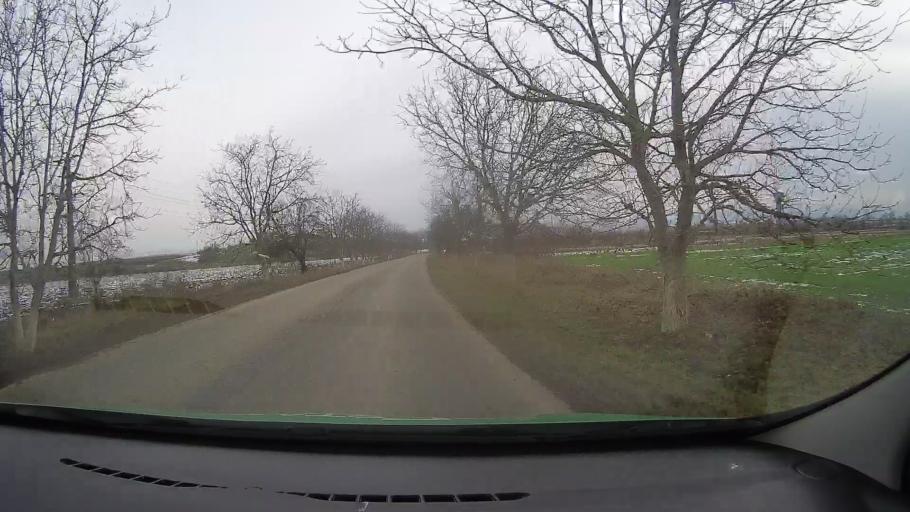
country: RO
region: Hunedoara
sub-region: Comuna Romos
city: Romos
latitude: 45.8815
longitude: 23.2555
